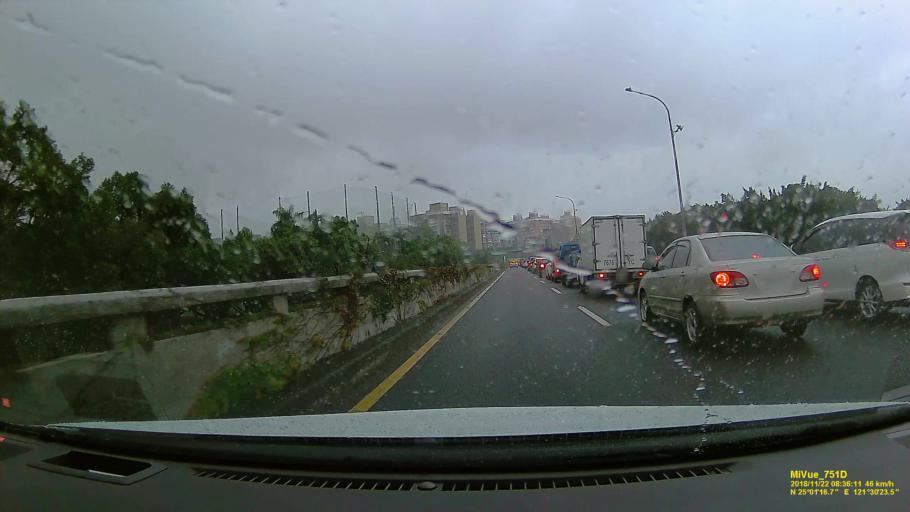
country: TW
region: Taipei
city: Taipei
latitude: 25.0214
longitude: 121.5067
